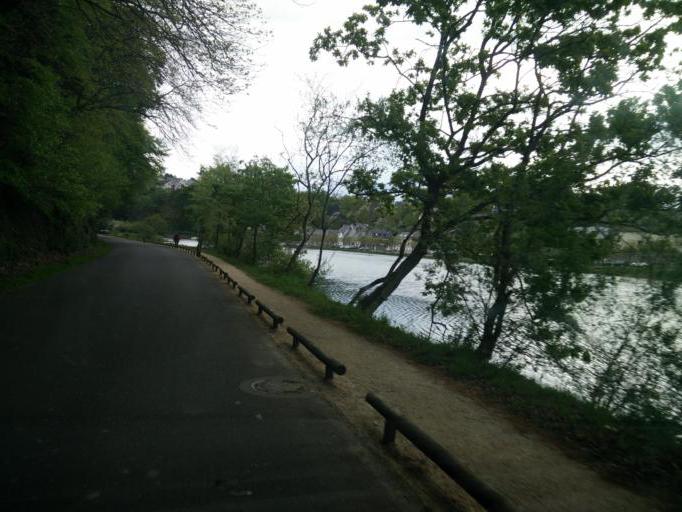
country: FR
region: Brittany
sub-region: Departement des Cotes-d'Armor
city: Lannion
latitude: 48.7357
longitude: -3.4701
